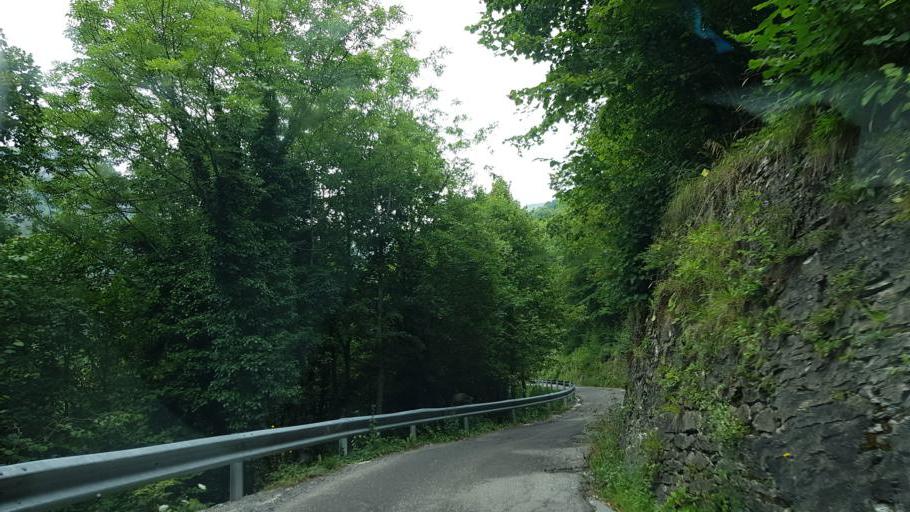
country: IT
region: Piedmont
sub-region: Provincia di Cuneo
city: Stroppo
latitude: 44.5108
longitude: 7.1259
